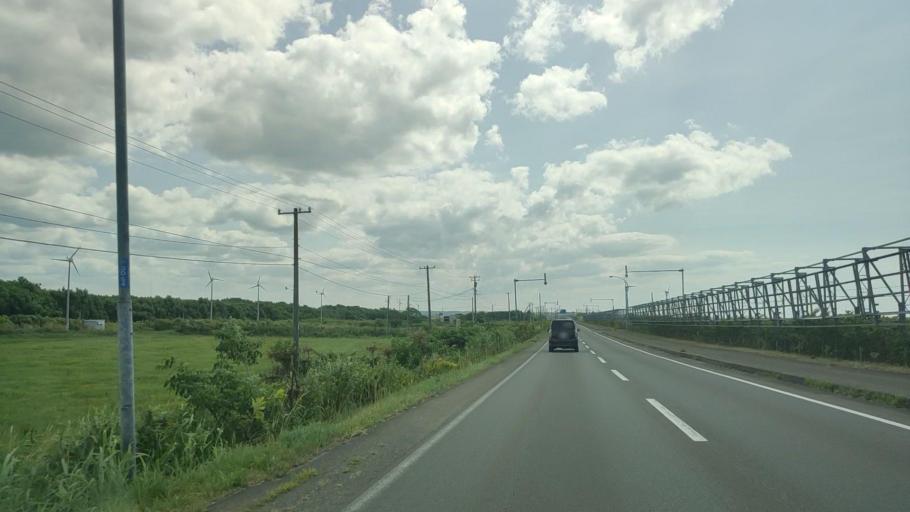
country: JP
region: Hokkaido
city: Makubetsu
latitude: 44.7599
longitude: 141.7942
